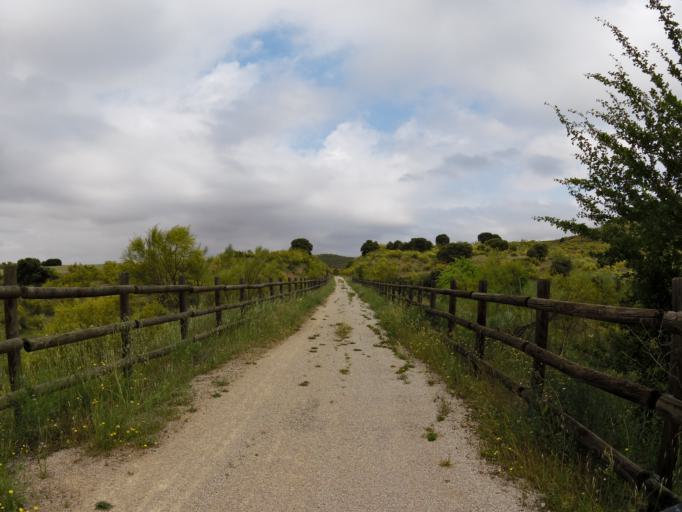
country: ES
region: Castille-La Mancha
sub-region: Provincia de Albacete
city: Alcaraz
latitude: 38.7033
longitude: -2.4850
